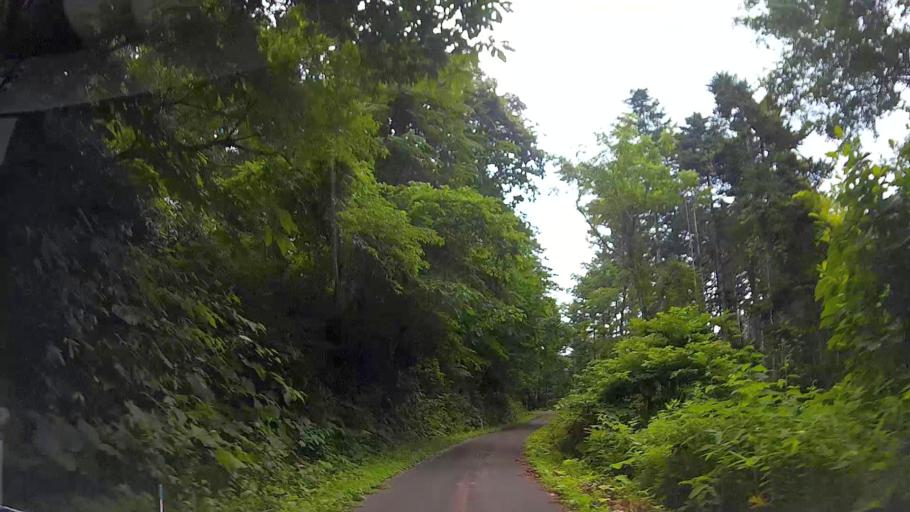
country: JP
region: Hokkaido
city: Nanae
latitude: 42.0510
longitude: 140.4938
